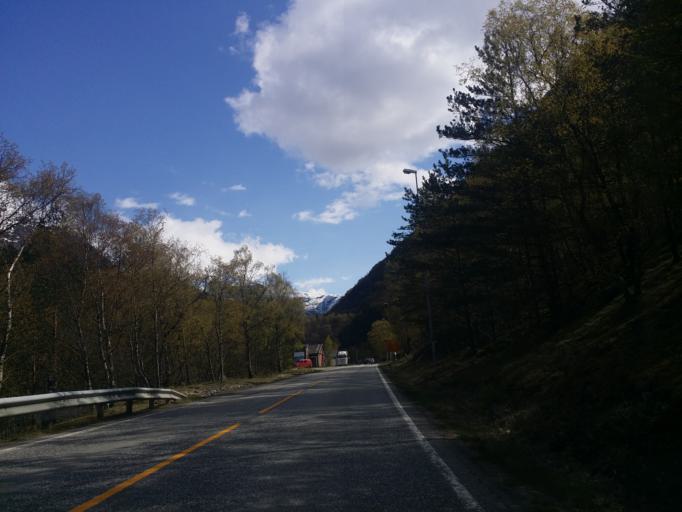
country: NO
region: Hordaland
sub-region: Eidfjord
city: Eidfjord
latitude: 60.4630
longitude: 7.0774
